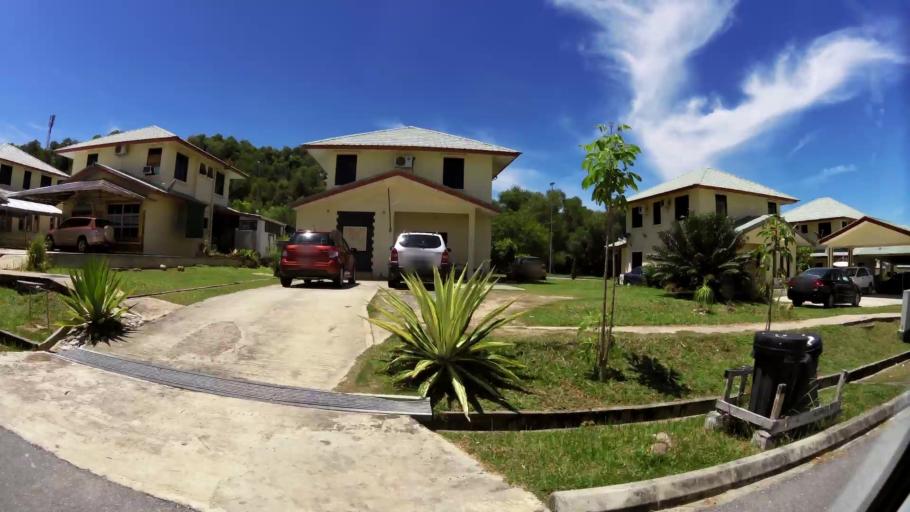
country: BN
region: Brunei and Muara
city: Bandar Seri Begawan
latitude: 5.0335
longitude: 115.0396
